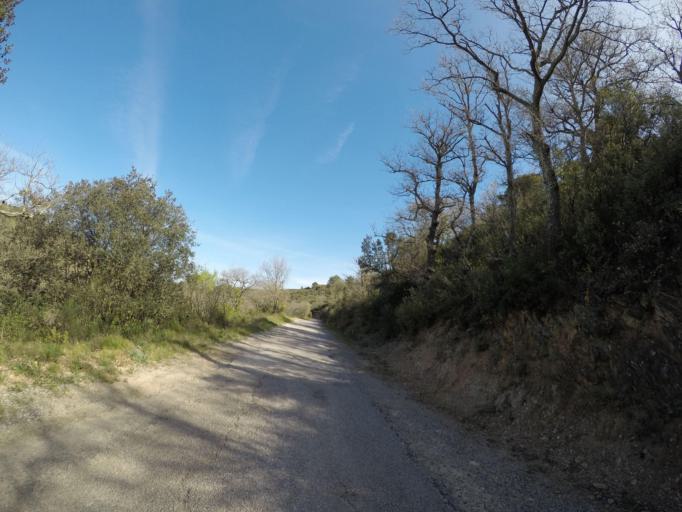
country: FR
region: Languedoc-Roussillon
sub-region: Departement des Pyrenees-Orientales
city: Thuir
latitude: 42.6311
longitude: 2.7013
